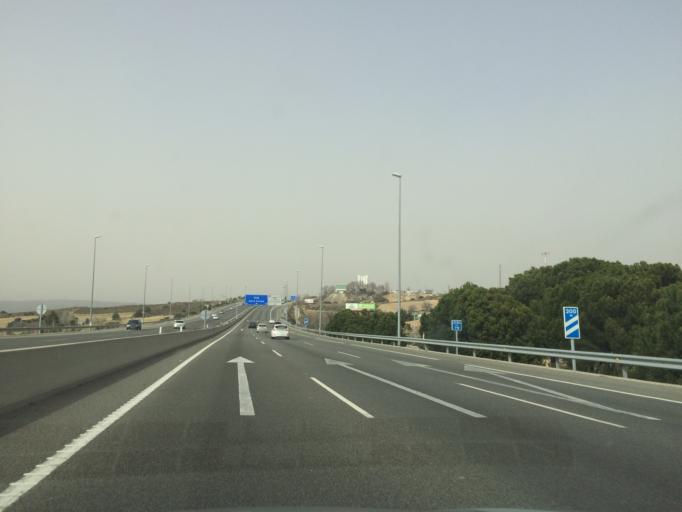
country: ES
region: Madrid
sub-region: Provincia de Madrid
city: Majadahonda
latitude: 40.4718
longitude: -3.8932
